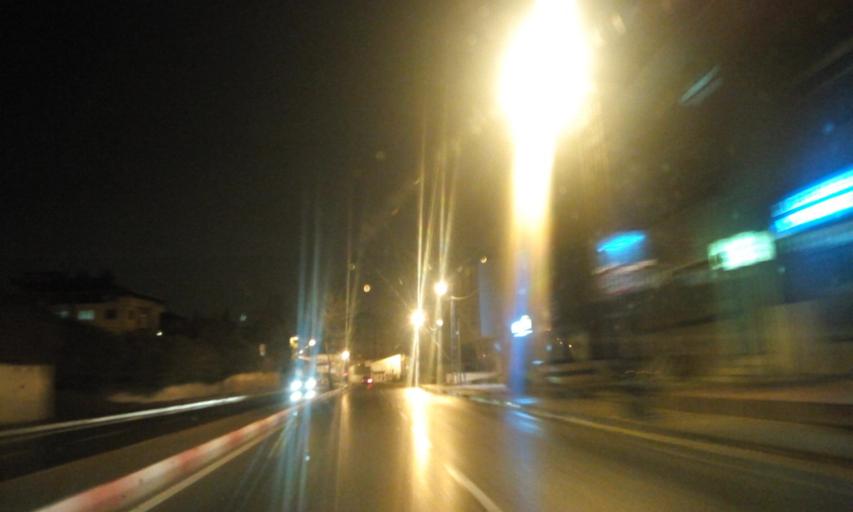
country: TR
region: Istanbul
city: Sultanbeyli
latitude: 40.9371
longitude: 29.2729
